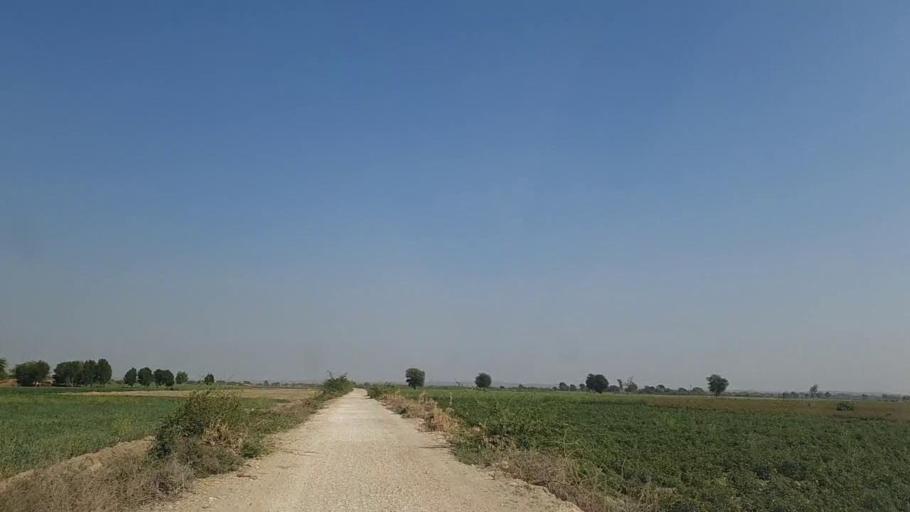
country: PK
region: Sindh
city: Naukot
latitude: 24.8991
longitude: 69.4645
